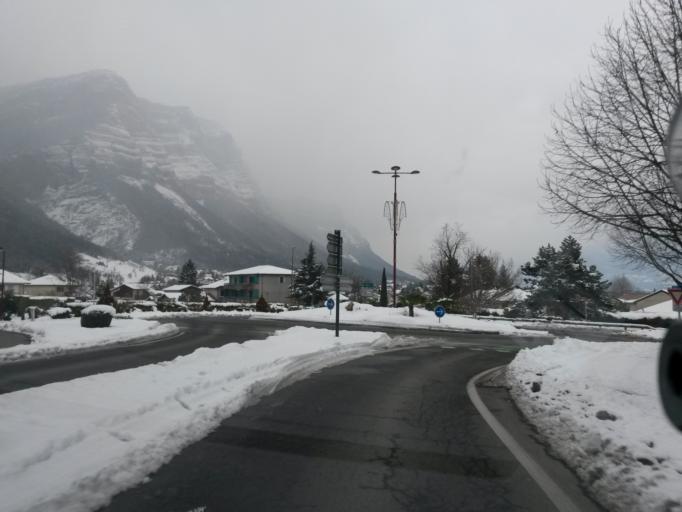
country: FR
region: Rhone-Alpes
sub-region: Departement de l'Isere
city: Crolles
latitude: 45.2765
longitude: 5.8723
